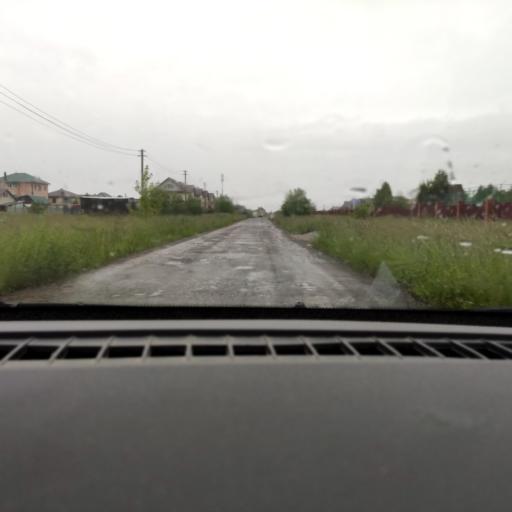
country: RU
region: Perm
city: Perm
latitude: 58.0384
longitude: 56.3721
